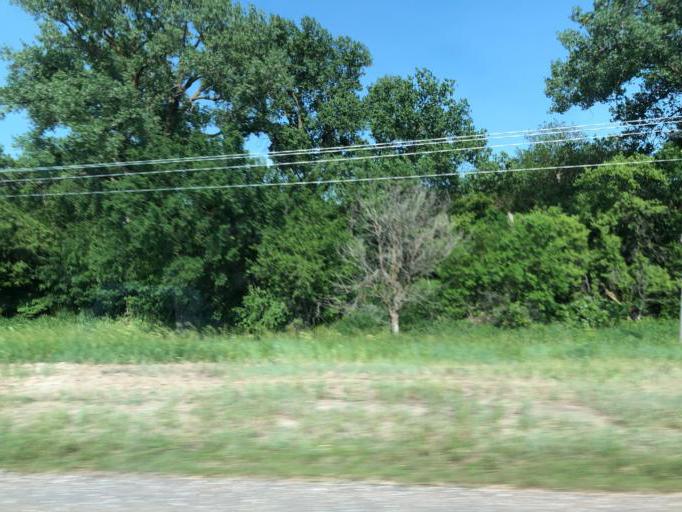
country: US
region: Nebraska
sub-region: York County
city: York
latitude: 40.7244
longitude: -97.5964
